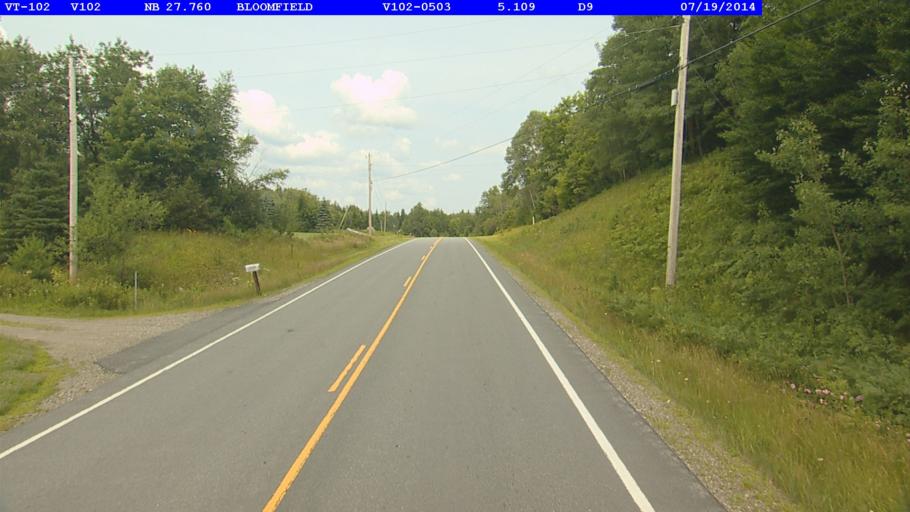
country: US
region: New Hampshire
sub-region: Coos County
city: Colebrook
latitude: 44.8042
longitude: -71.5730
